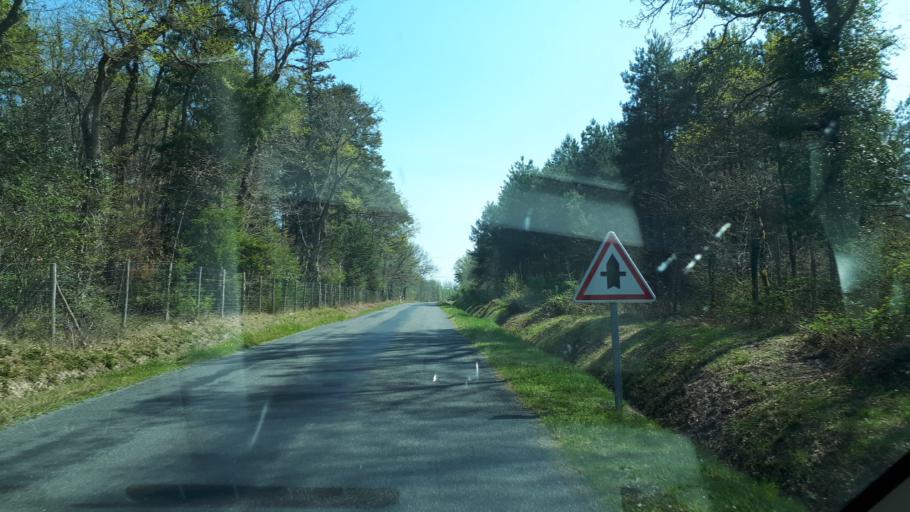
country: FR
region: Centre
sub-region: Departement du Cher
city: Neuvy-sur-Barangeon
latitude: 47.3202
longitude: 2.1811
